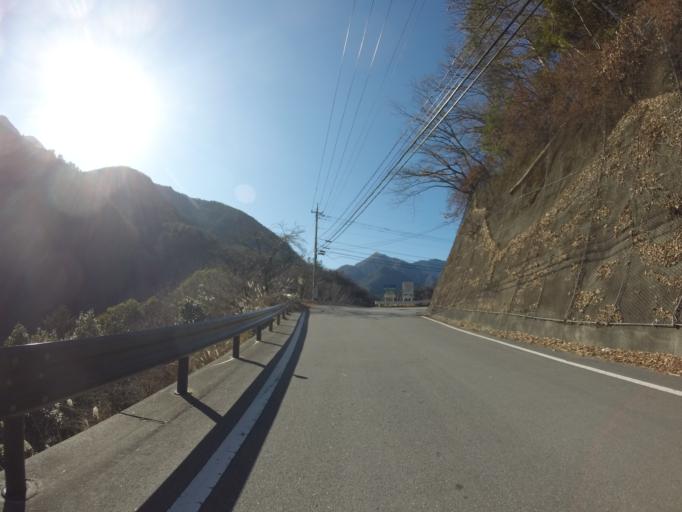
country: JP
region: Yamanashi
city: Ryuo
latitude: 35.4141
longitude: 138.3476
